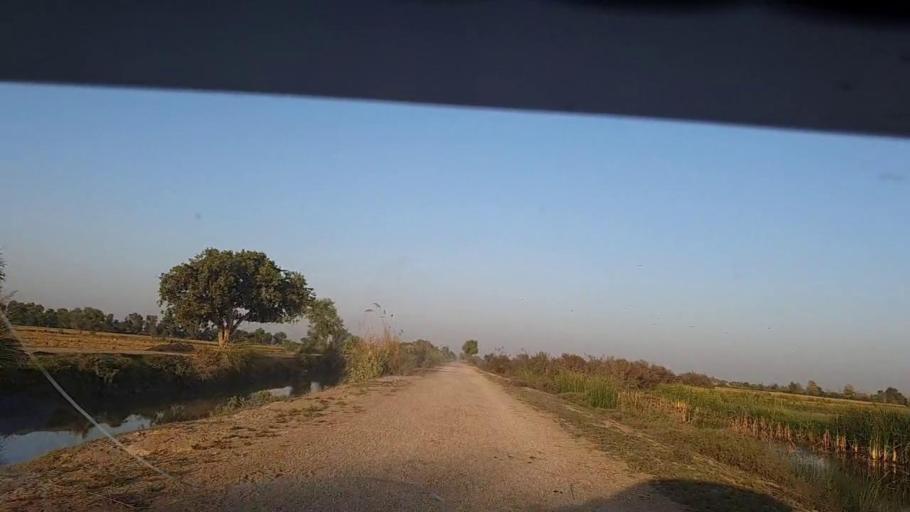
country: PK
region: Sindh
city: Ratodero
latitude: 27.8849
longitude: 68.2117
